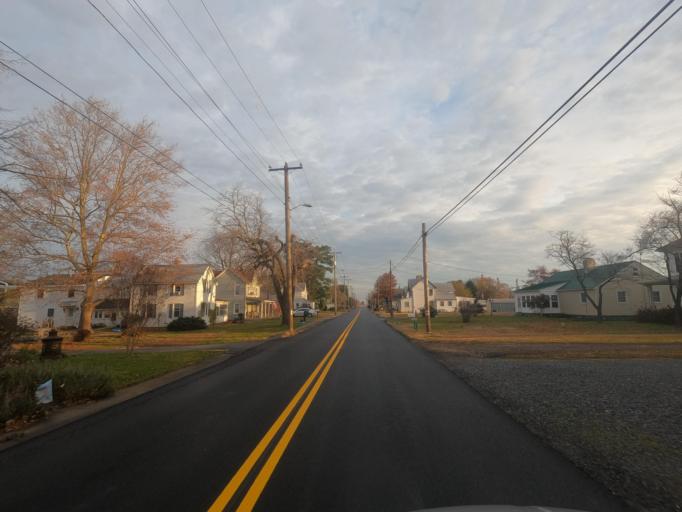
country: US
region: Delaware
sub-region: New Castle County
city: Townsend
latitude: 39.3071
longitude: -75.8268
